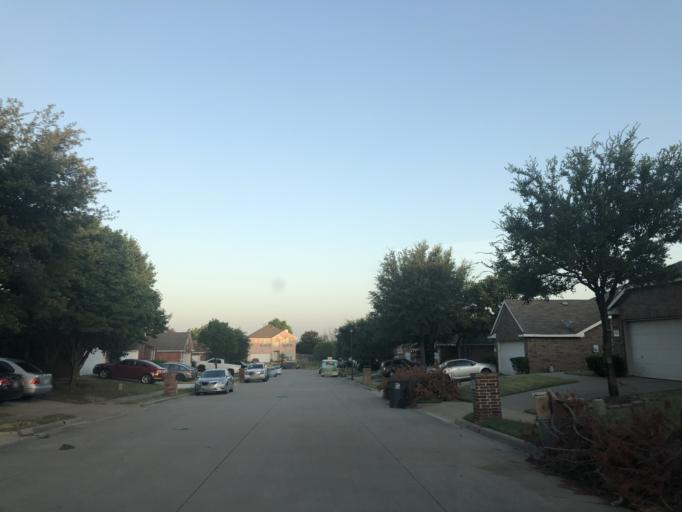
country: US
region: Texas
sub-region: Dallas County
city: Duncanville
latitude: 32.6553
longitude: -96.9622
